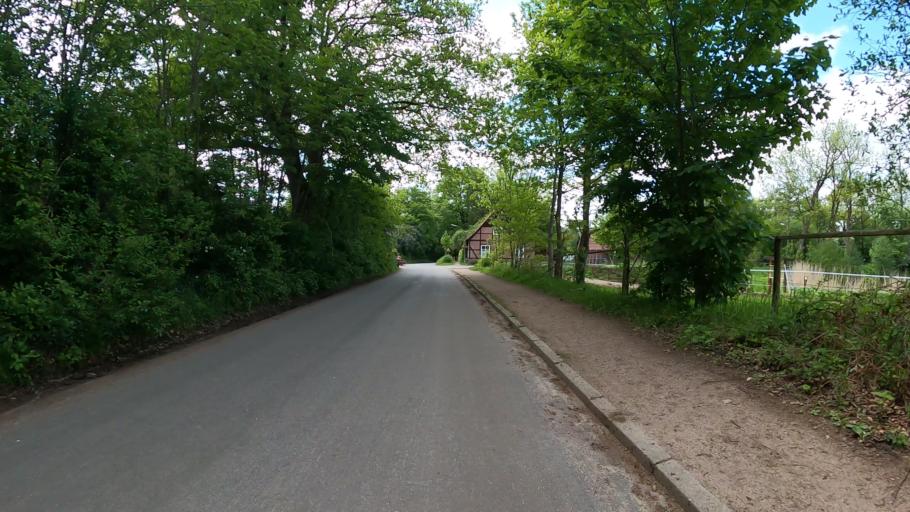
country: DE
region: Hamburg
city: Wohldorf-Ohlstedt
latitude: 53.7109
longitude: 10.1370
